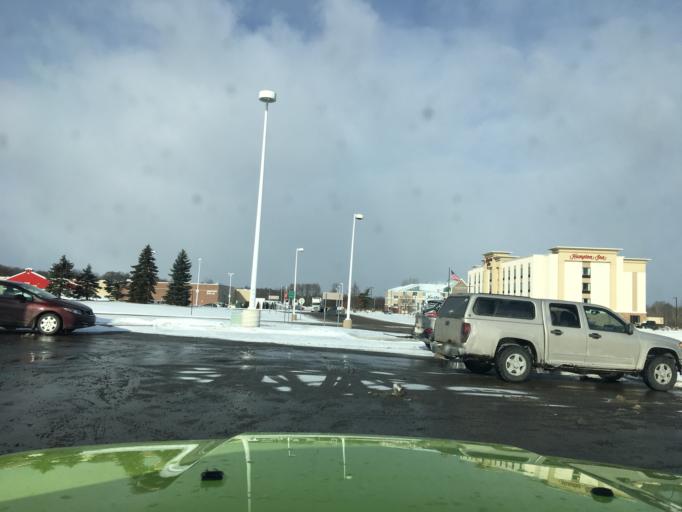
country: US
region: Michigan
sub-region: Mecosta County
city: Big Rapids
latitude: 43.6885
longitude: -85.5154
